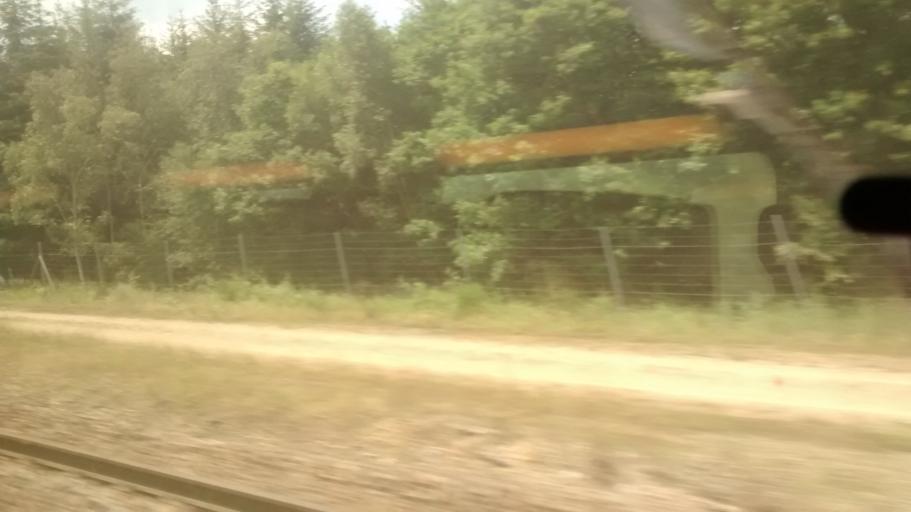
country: FR
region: Bourgogne
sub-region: Departement de Saone-et-Loire
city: Saint-Gengoux-le-National
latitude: 46.6004
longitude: 4.6079
